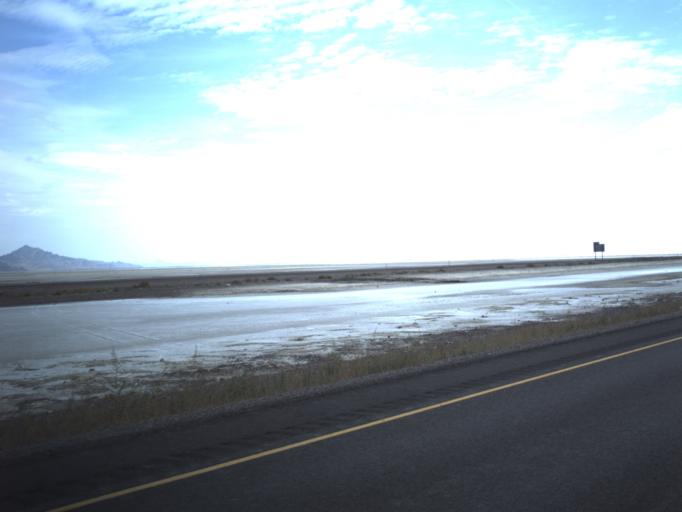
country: US
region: Utah
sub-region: Tooele County
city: Wendover
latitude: 40.7404
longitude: -113.9466
